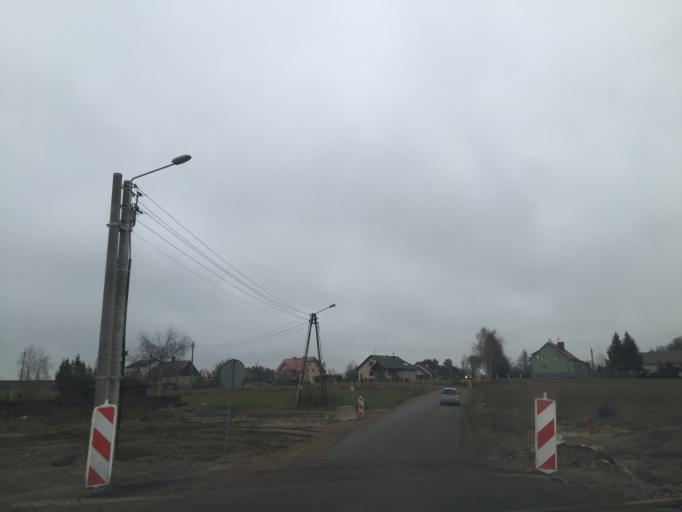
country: PL
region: Pomeranian Voivodeship
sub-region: Powiat kartuski
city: Banino
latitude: 54.3917
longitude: 18.4299
